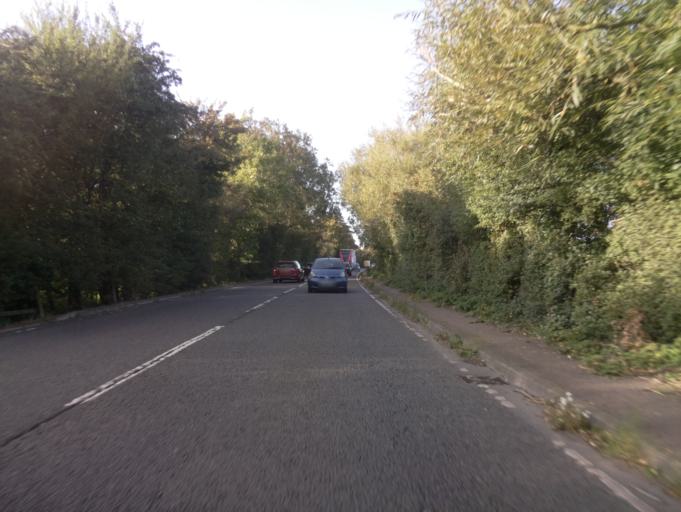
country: GB
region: England
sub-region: Gloucestershire
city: Gloucester
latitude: 51.8794
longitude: -2.2668
